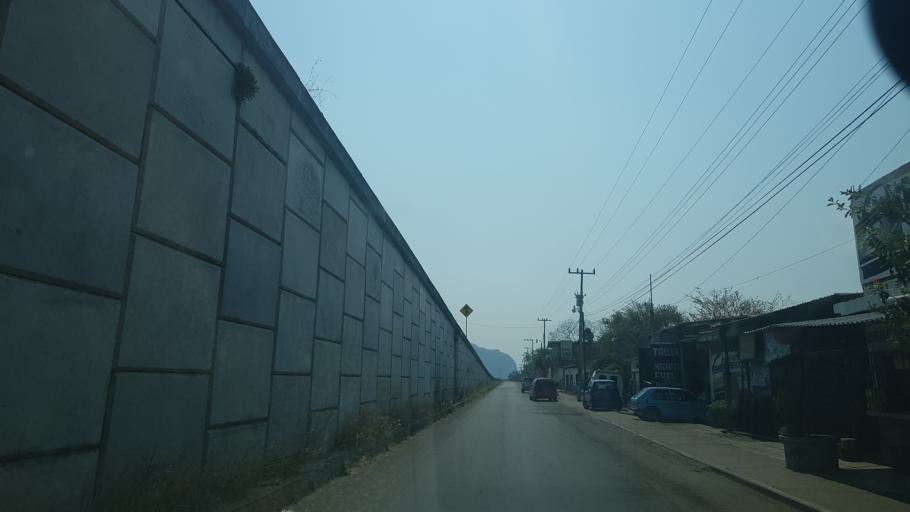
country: MX
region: Morelos
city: Amayuca
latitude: 18.7171
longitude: -98.7940
